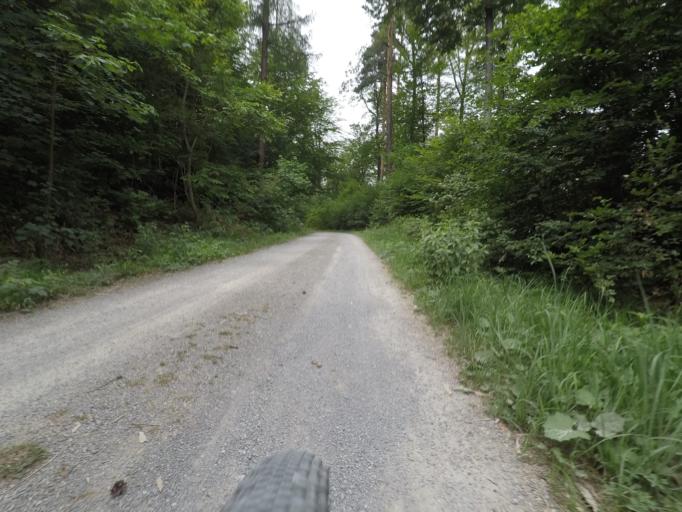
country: DE
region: Baden-Wuerttemberg
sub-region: Regierungsbezirk Stuttgart
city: Hildrizhausen
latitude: 48.5754
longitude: 8.9747
